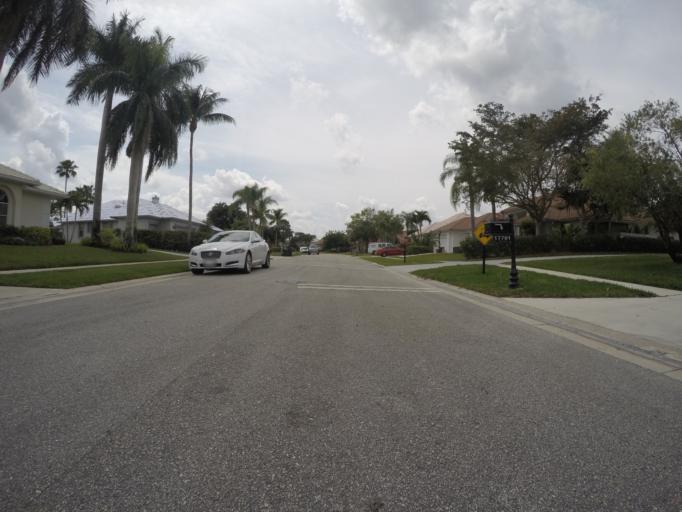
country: US
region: Florida
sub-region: Palm Beach County
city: Villages of Oriole
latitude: 26.4127
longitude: -80.2167
